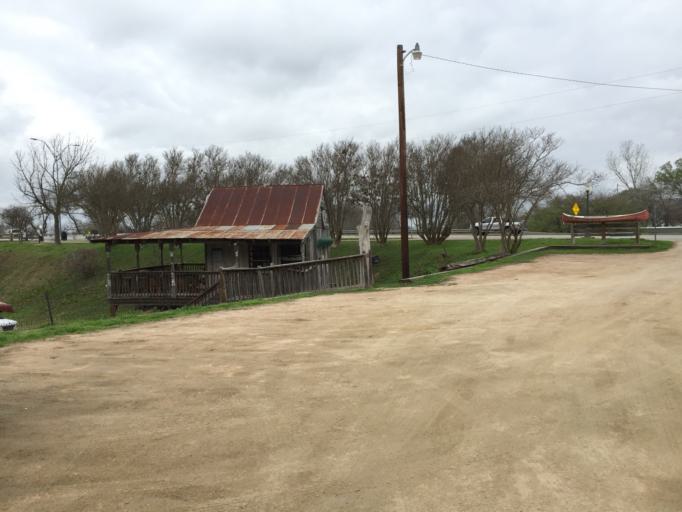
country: US
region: Texas
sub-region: Bastrop County
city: Bastrop
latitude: 30.1101
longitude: -97.3208
